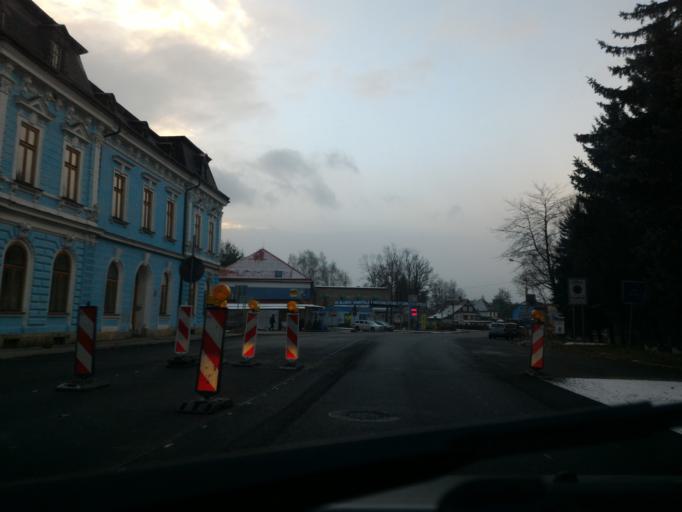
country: DE
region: Saxony
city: Seifhennersdorf
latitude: 50.9214
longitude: 14.6073
